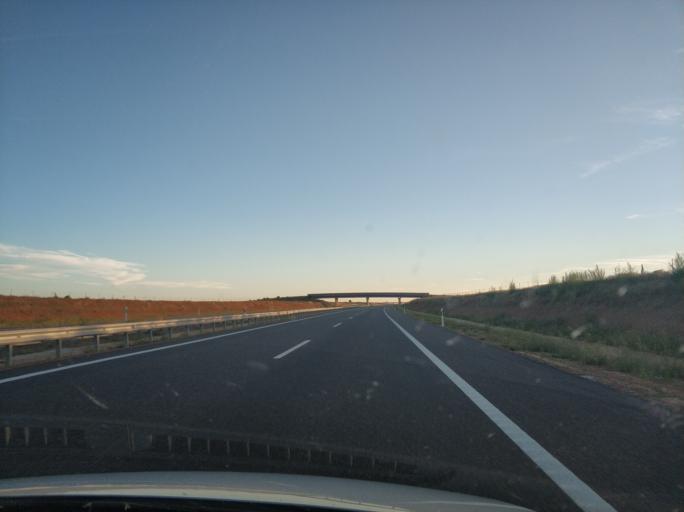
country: ES
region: Castille and Leon
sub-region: Provincia de Zamora
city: Castrogonzalo
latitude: 41.9552
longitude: -5.6180
